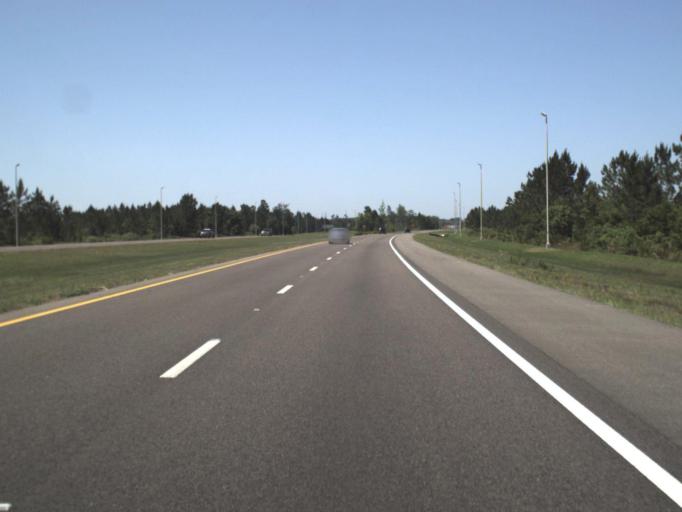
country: US
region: Florida
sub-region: Duval County
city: Baldwin
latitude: 30.2850
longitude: -81.8784
